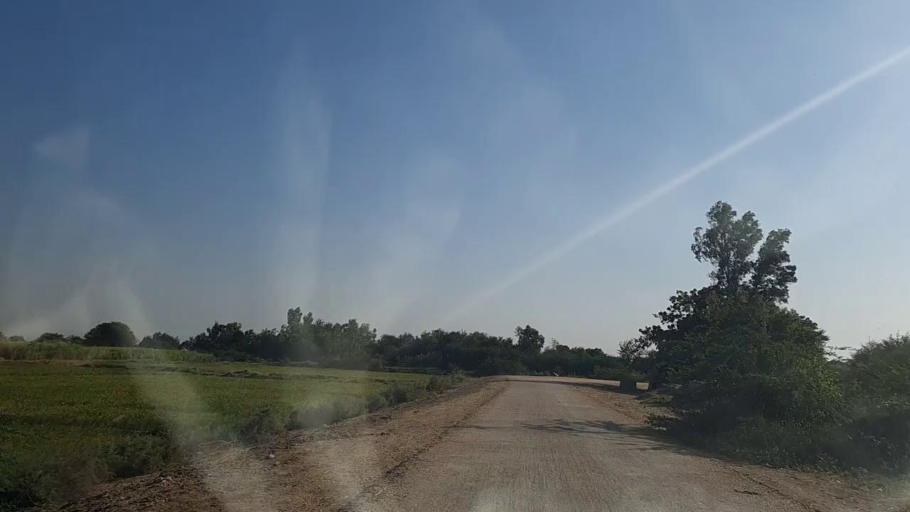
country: PK
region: Sindh
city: Mirpur Batoro
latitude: 24.5543
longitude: 68.1723
